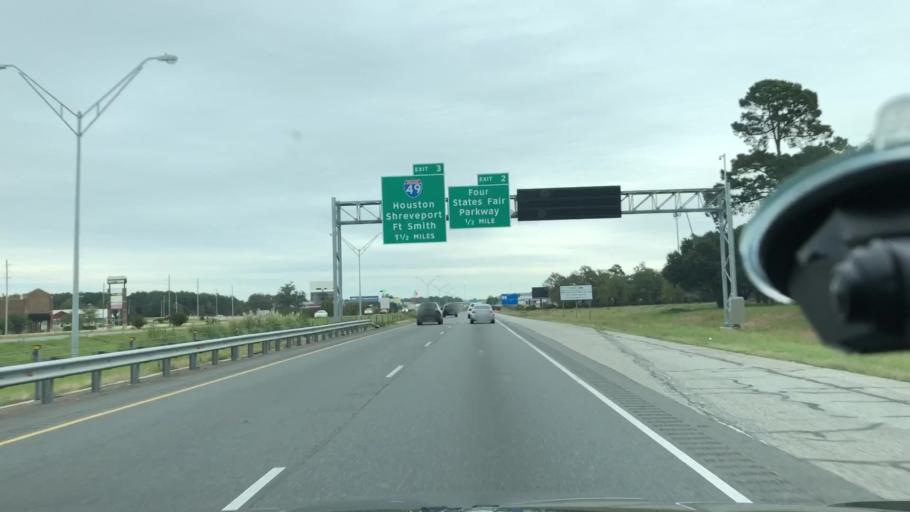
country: US
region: Arkansas
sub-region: Miller County
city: Texarkana
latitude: 33.4729
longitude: -94.0209
